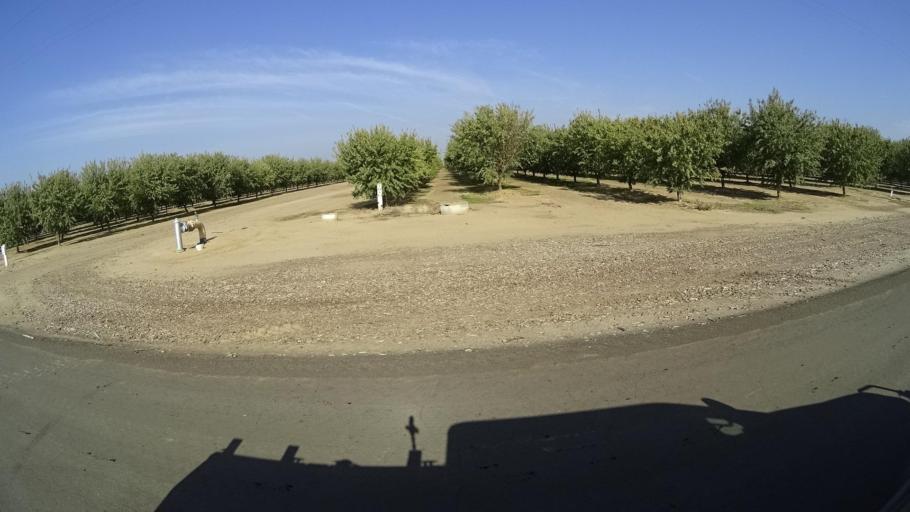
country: US
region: California
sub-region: Kern County
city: McFarland
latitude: 35.6601
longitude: -119.1779
